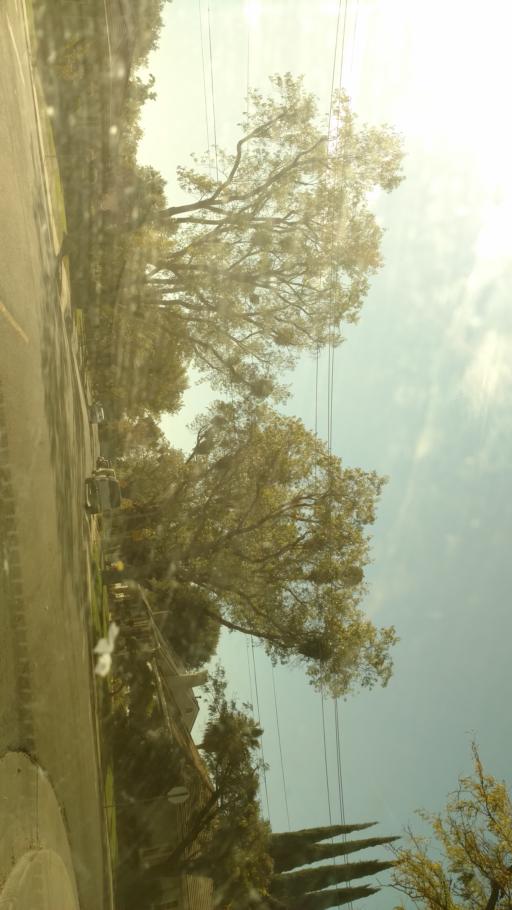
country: US
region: California
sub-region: San Joaquin County
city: Stockton
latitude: 37.9701
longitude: -121.3112
